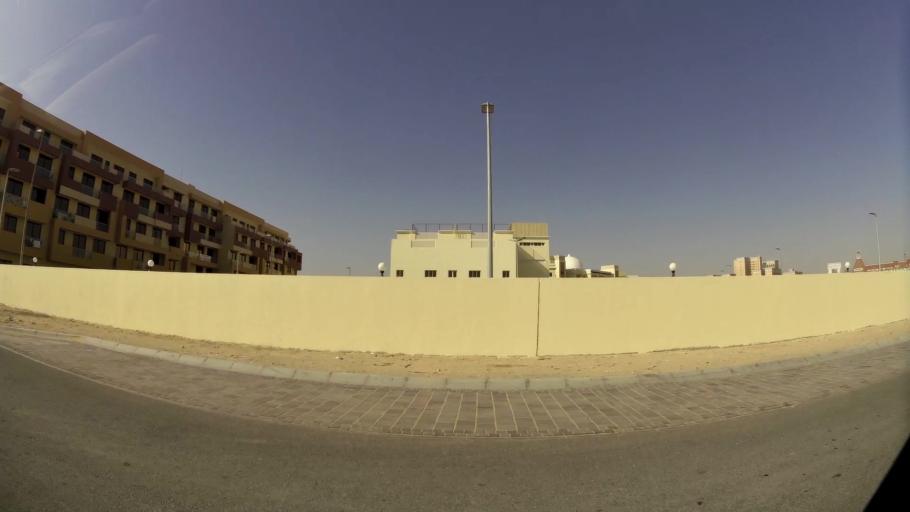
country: AE
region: Dubai
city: Dubai
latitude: 25.0650
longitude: 55.2031
